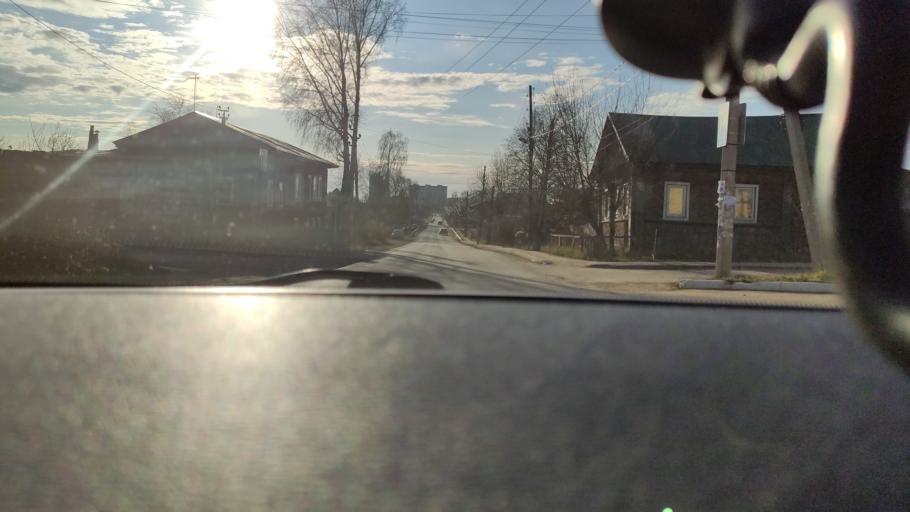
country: RU
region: Perm
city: Kondratovo
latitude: 58.0521
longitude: 56.0289
